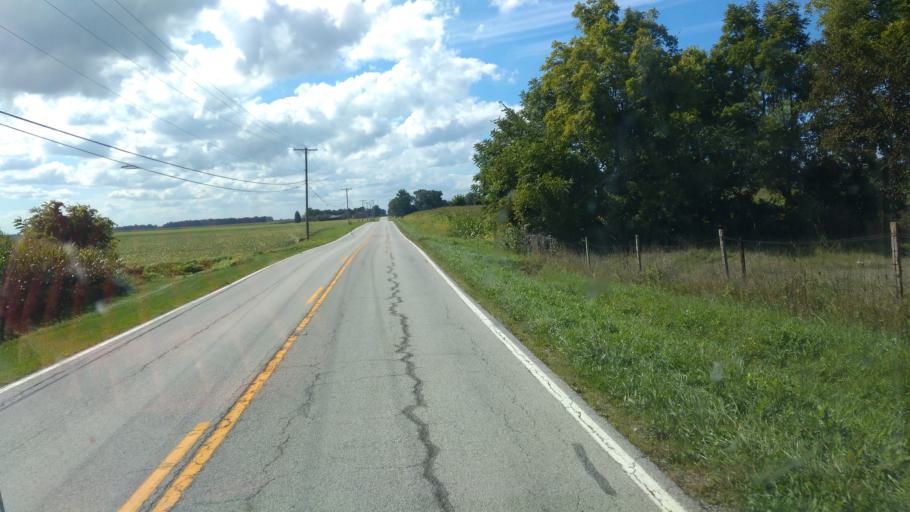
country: US
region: Ohio
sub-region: Huron County
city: Bellevue
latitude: 41.3866
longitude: -82.8840
